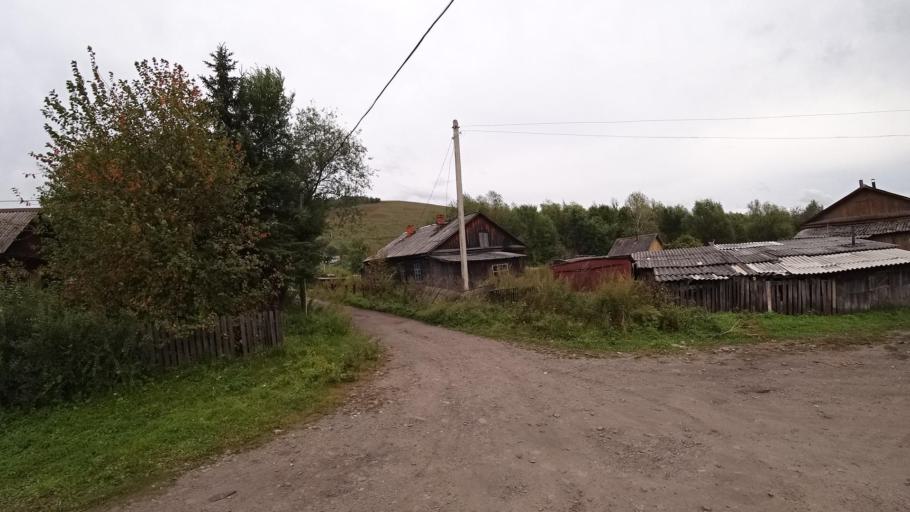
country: RU
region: Jewish Autonomous Oblast
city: Khingansk
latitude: 49.0279
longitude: 131.0532
